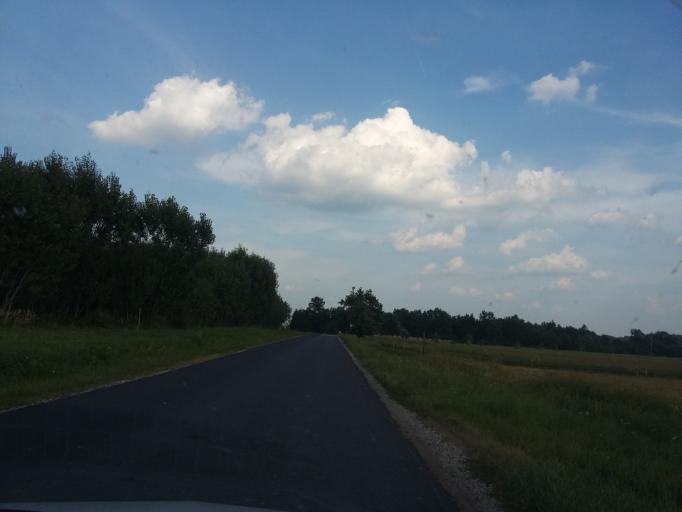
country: SI
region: Hodos-Hodos
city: Hodos
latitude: 46.8501
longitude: 16.3938
